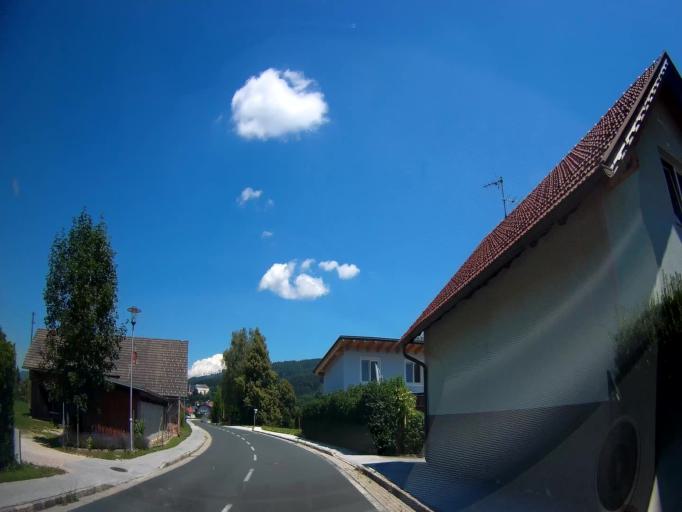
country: AT
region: Carinthia
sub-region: Politischer Bezirk Volkermarkt
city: Bleiburg/Pliberk
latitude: 46.5796
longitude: 14.7935
